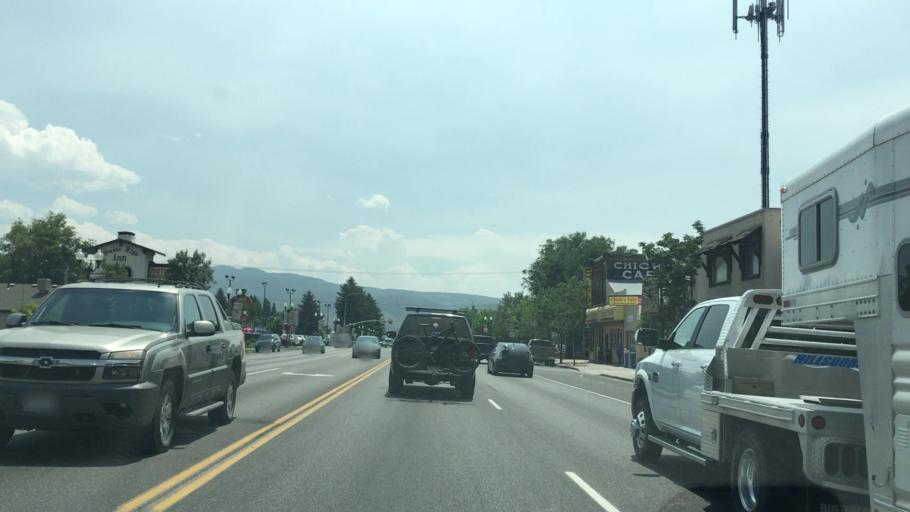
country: US
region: Utah
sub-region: Wasatch County
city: Heber
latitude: 40.5062
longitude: -111.4136
